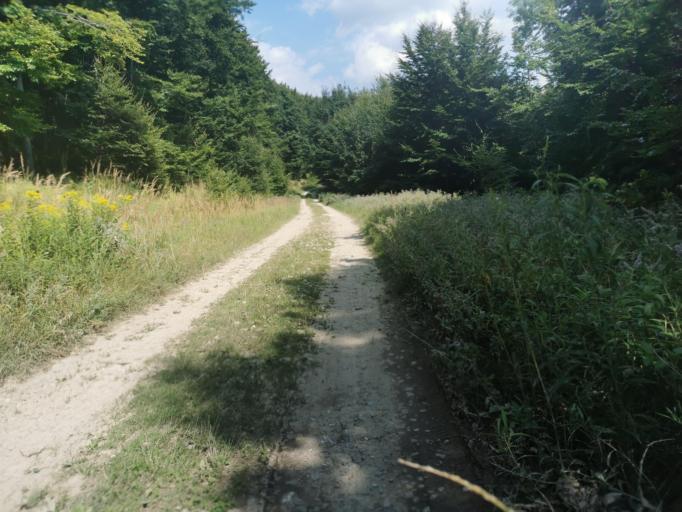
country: SK
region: Trenciansky
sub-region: Okres Myjava
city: Myjava
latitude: 48.8229
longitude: 17.5849
